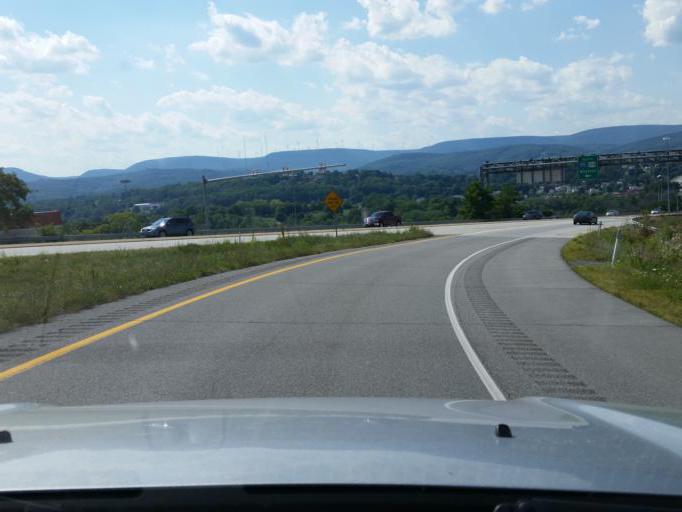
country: US
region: Pennsylvania
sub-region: Blair County
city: Lakemont
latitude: 40.4921
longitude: -78.3818
